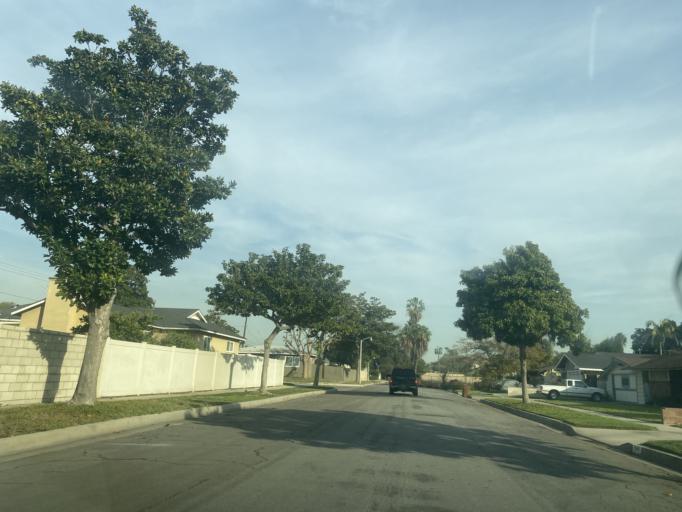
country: US
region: California
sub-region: Orange County
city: Buena Park
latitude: 33.8572
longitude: -117.9637
